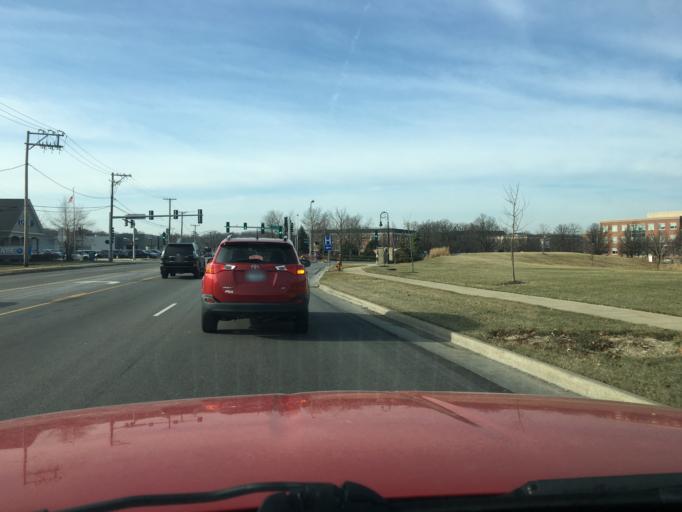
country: US
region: Illinois
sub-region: DuPage County
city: Oak Brook
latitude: 41.8177
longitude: -87.9196
